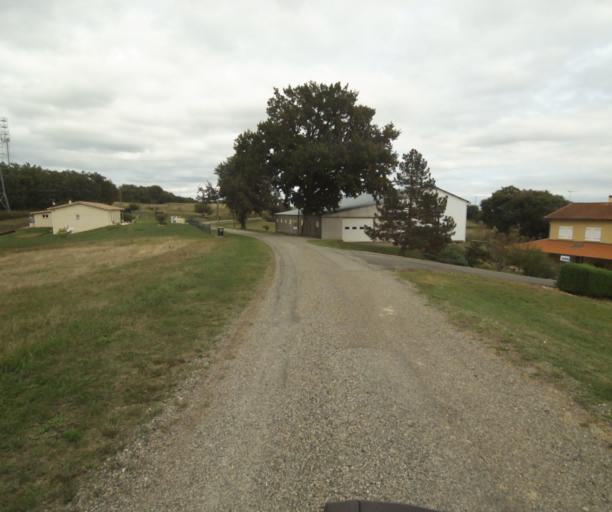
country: FR
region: Midi-Pyrenees
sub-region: Departement du Tarn-et-Garonne
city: Beaumont-de-Lomagne
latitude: 43.8524
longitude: 1.1034
